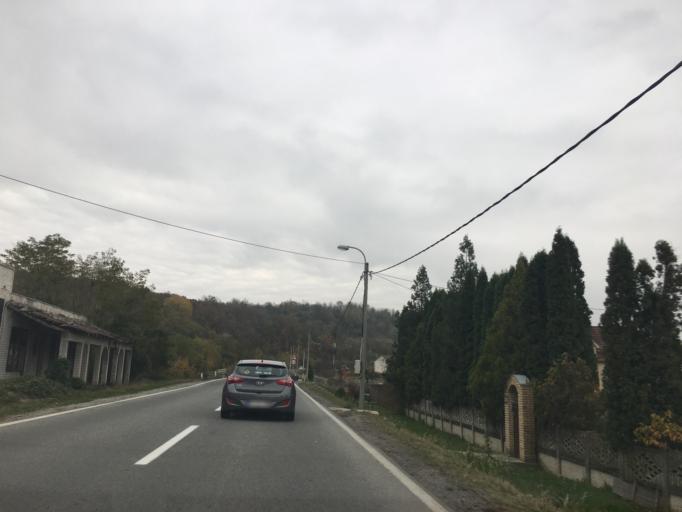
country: RS
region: Central Serbia
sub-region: Raski Okrug
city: Kraljevo
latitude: 43.7176
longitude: 20.7813
